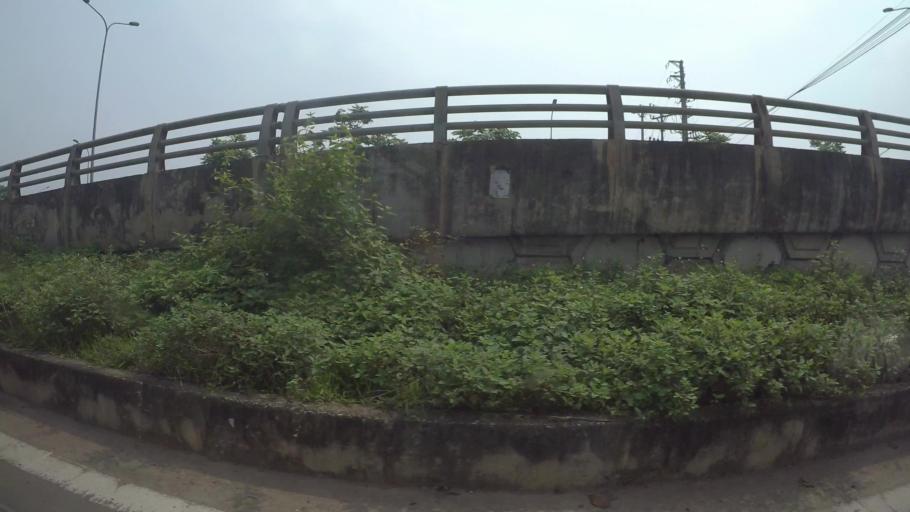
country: VN
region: Ha Noi
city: Lien Quan
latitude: 20.9914
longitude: 105.5361
